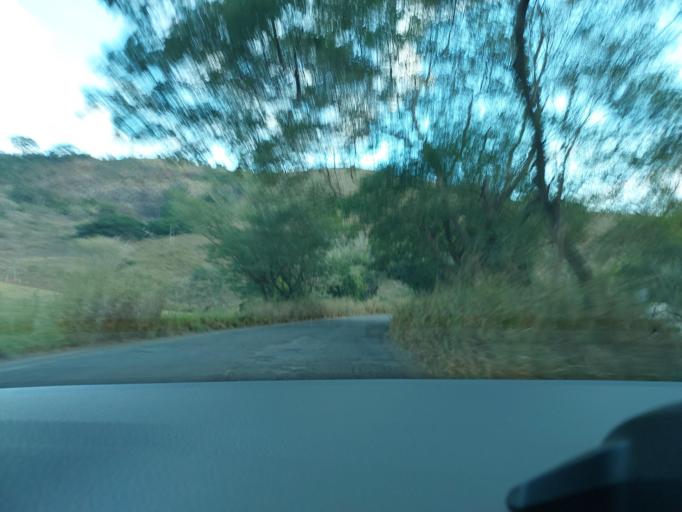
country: BR
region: Rio de Janeiro
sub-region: Natividade
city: Natividade
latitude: -21.1984
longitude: -42.1171
